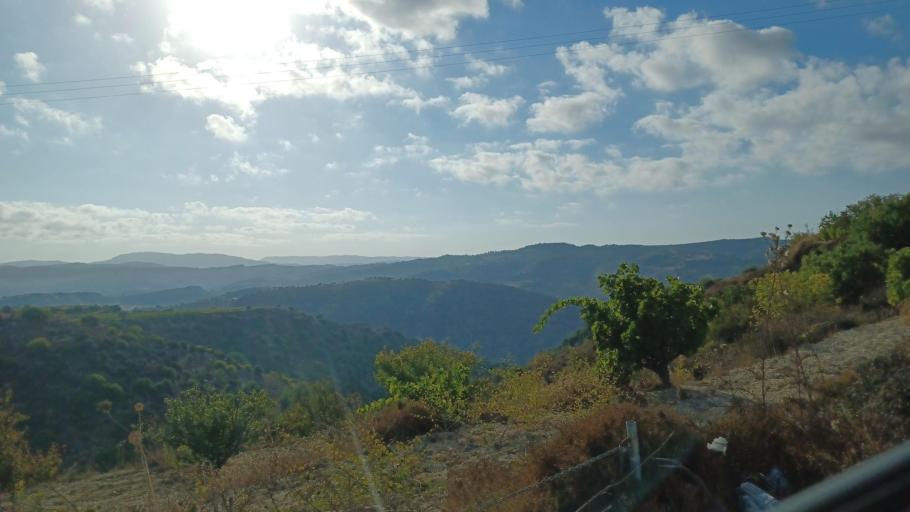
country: CY
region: Pafos
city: Mesogi
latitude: 34.8309
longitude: 32.5238
